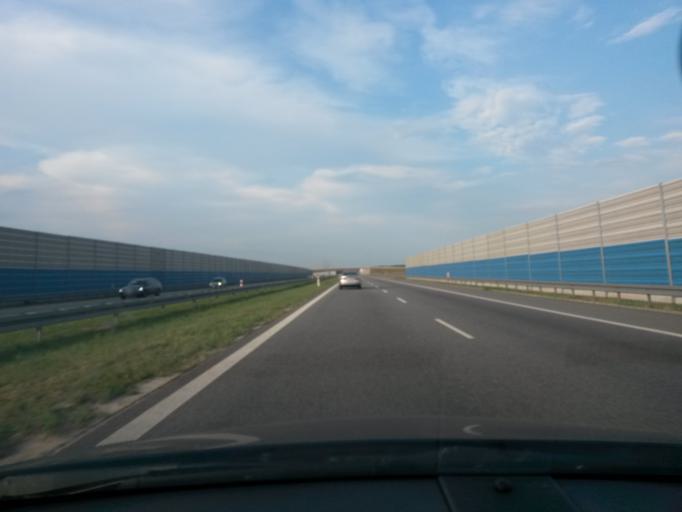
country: PL
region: Lodz Voivodeship
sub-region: Powiat brzezinski
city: Dmosin
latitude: 51.9421
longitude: 19.8243
